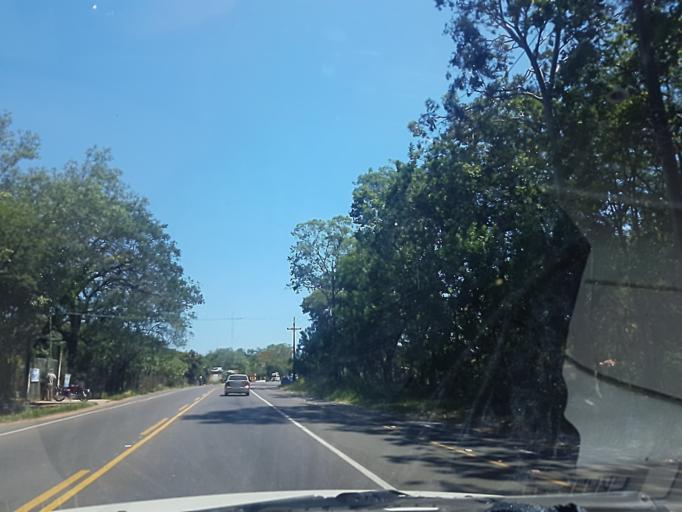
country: PY
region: Central
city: Limpio
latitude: -25.2195
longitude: -57.4176
